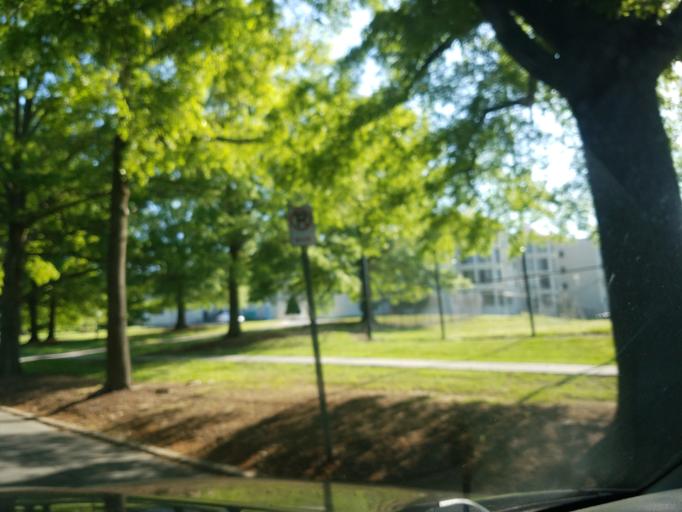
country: US
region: North Carolina
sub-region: Durham County
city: Durham
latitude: 36.0202
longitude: -78.9190
